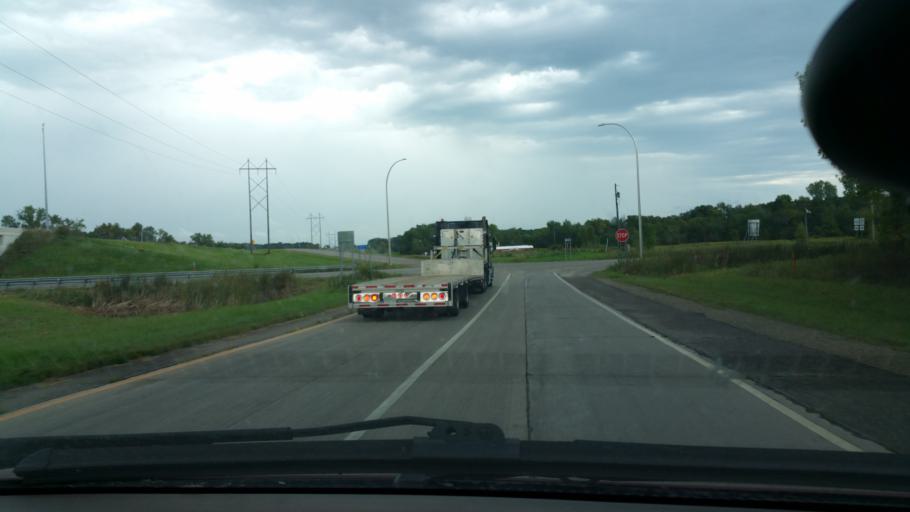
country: US
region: Minnesota
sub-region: Rice County
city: Dundas
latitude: 44.4712
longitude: -93.2914
